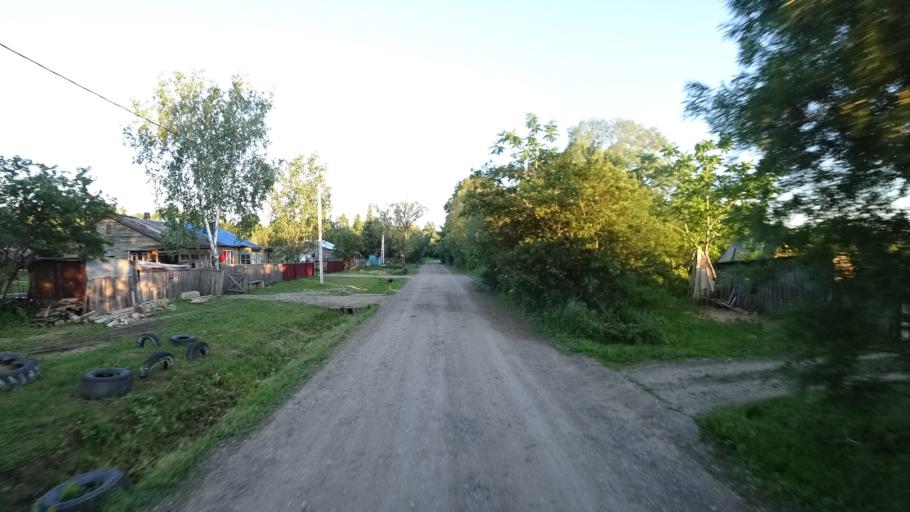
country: RU
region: Khabarovsk Krai
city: Khor
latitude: 47.8509
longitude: 134.9835
